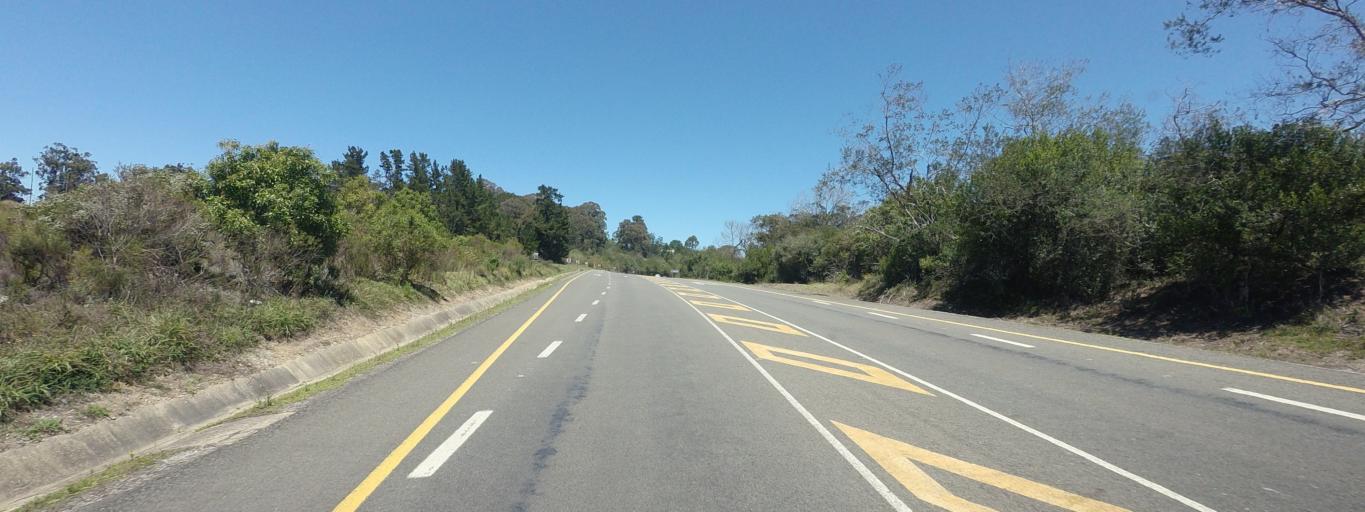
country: ZA
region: Western Cape
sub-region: Eden District Municipality
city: Plettenberg Bay
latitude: -33.9670
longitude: 23.4486
